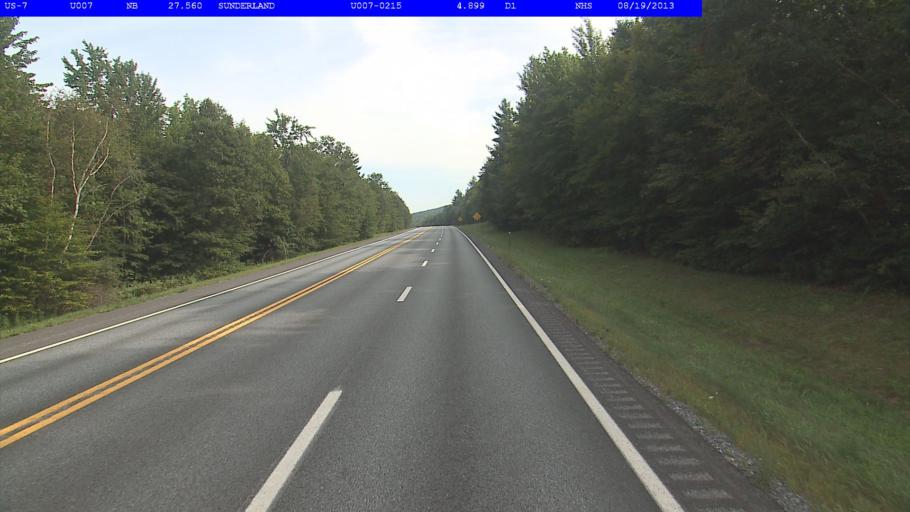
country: US
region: Vermont
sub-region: Bennington County
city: Arlington
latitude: 43.0899
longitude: -73.1028
